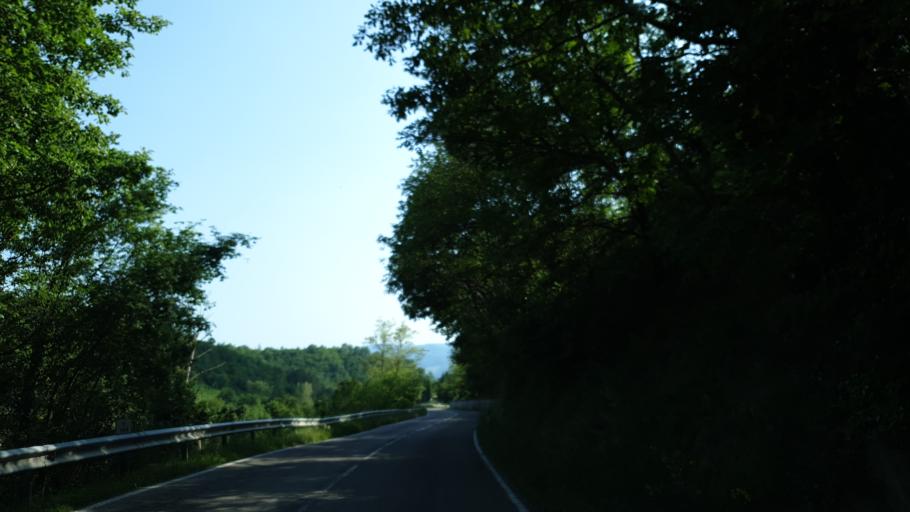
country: IT
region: Tuscany
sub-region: Province of Arezzo
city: Soci
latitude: 43.7557
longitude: 11.8277
